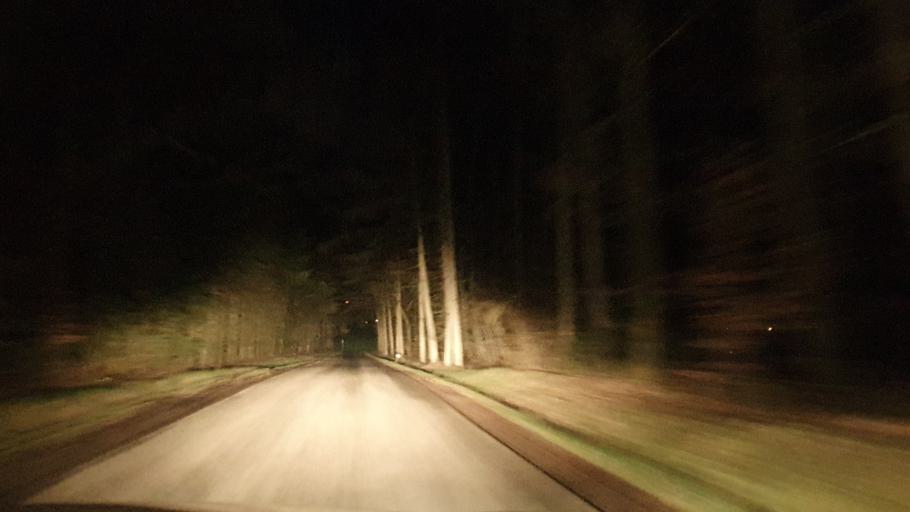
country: DE
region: Rheinland-Pfalz
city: Ratzert
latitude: 50.6427
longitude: 7.6409
